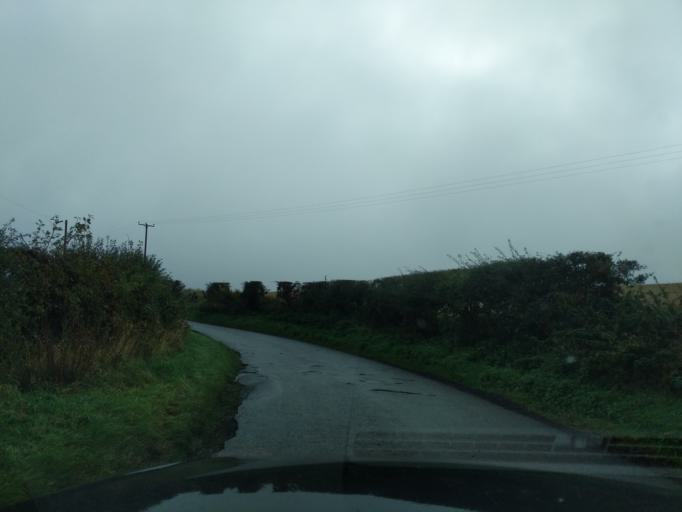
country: GB
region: Scotland
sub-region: East Lothian
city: Dunbar
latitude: 55.9456
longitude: -2.4036
